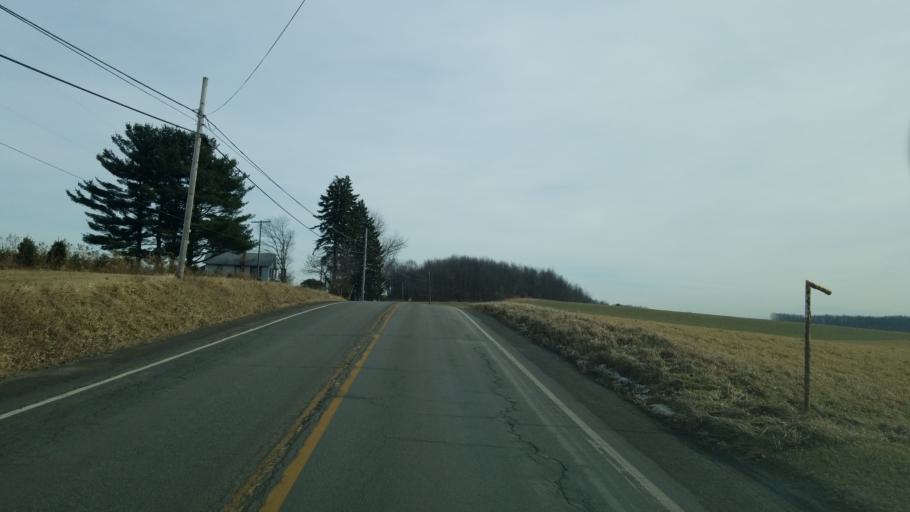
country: US
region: Pennsylvania
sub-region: Indiana County
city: Clymer
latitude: 40.7351
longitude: -78.9252
